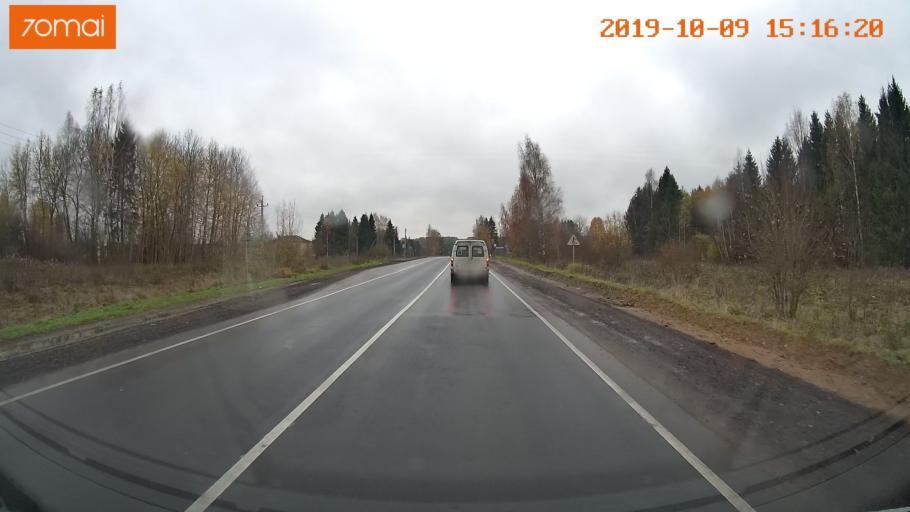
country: RU
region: Kostroma
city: Susanino
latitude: 58.1111
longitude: 41.5862
